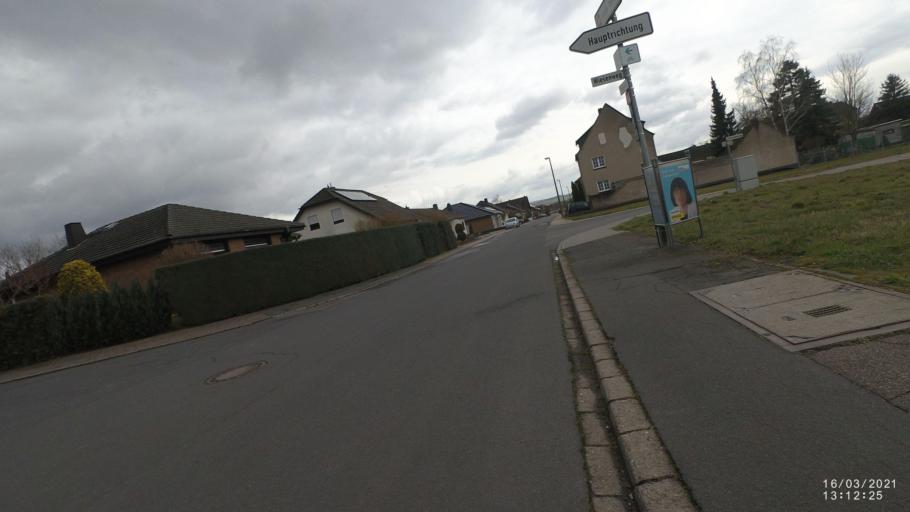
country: DE
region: Rheinland-Pfalz
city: Mendig
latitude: 50.3673
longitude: 7.2873
